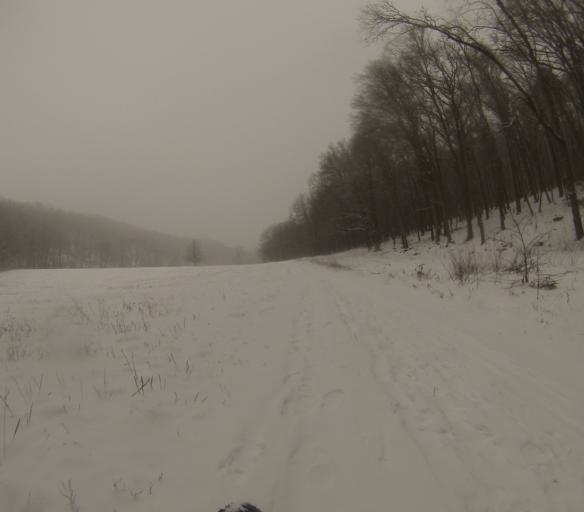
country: CZ
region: South Moravian
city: Strelice
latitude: 49.1331
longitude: 16.5058
